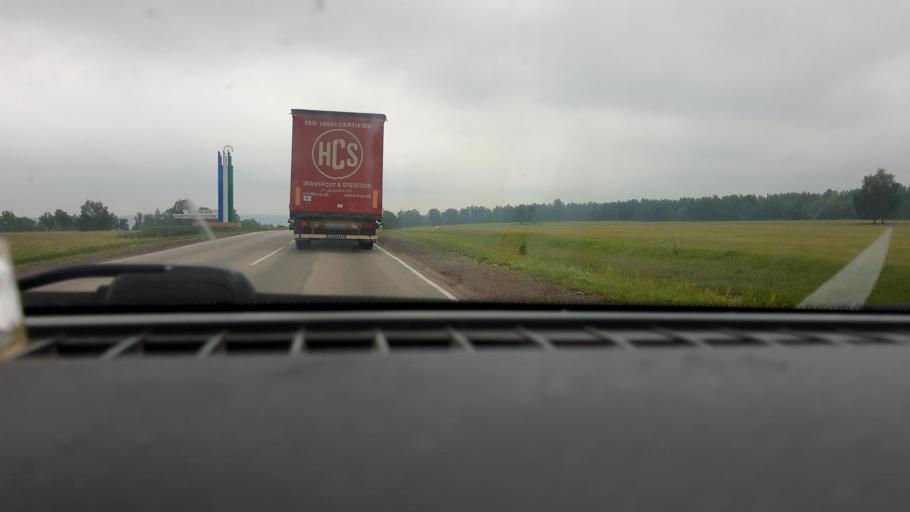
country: RU
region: Bashkortostan
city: Belebey
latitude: 54.2734
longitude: 54.0674
